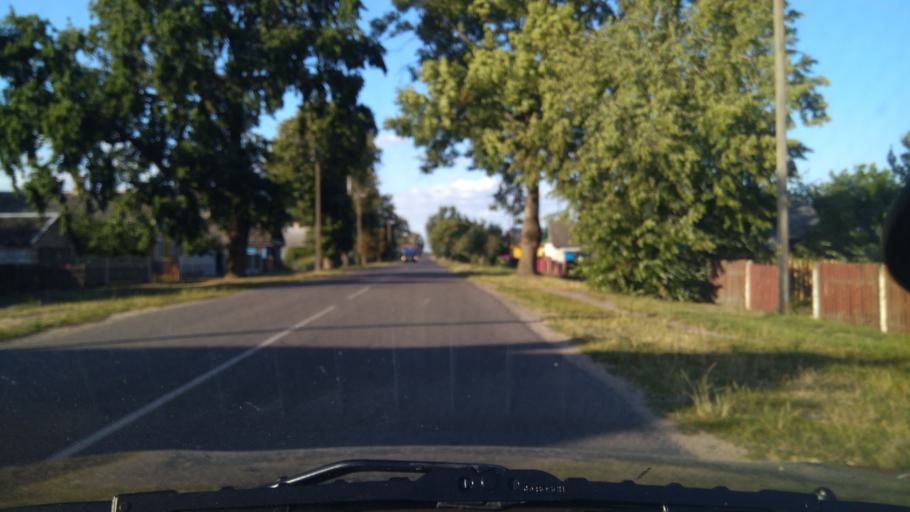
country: BY
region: Brest
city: Byaroza
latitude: 52.5840
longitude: 24.8636
